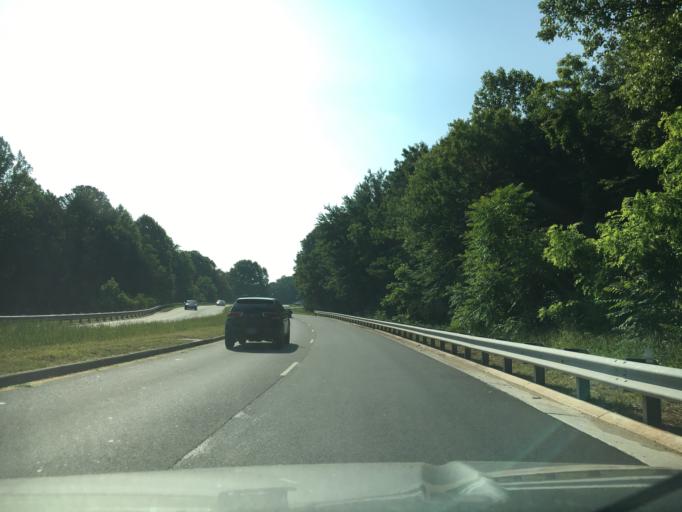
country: US
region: Virginia
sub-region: Campbell County
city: Timberlake
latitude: 37.3326
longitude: -79.2127
